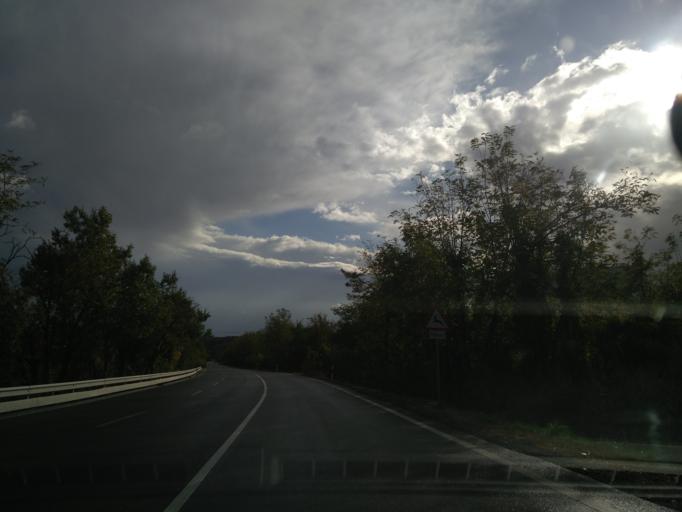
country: HU
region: Pest
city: Kerepes
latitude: 47.5787
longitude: 19.2913
